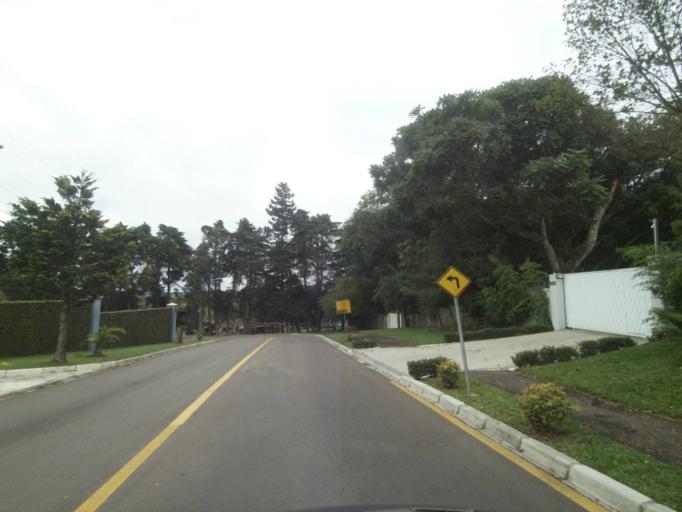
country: BR
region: Parana
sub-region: Curitiba
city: Curitiba
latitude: -25.4668
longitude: -49.3304
